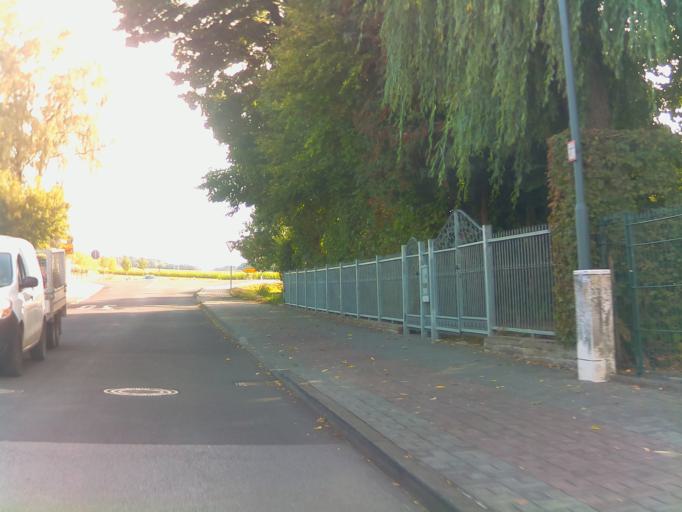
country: DE
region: Hesse
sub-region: Regierungsbezirk Kassel
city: Kunzell
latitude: 50.5251
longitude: 9.7477
